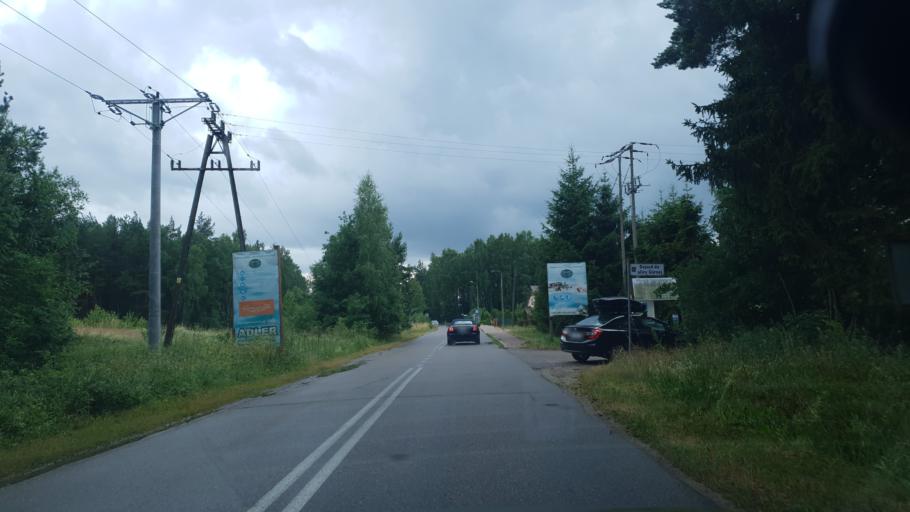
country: PL
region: Pomeranian Voivodeship
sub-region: Powiat kartuski
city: Stezyca
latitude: 54.2470
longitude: 18.0017
